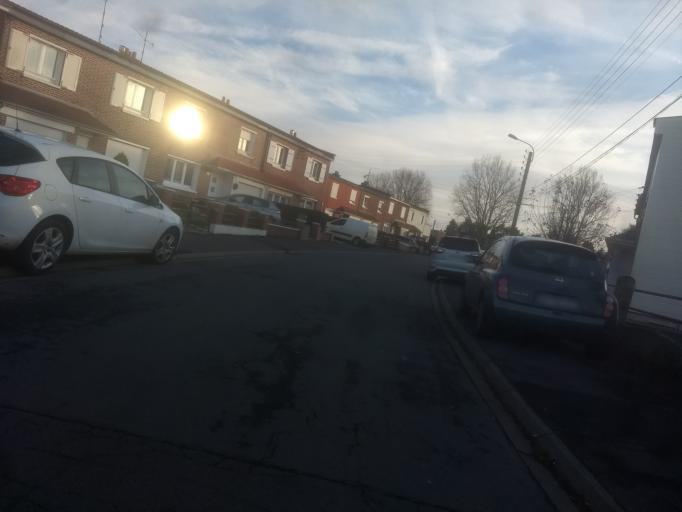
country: FR
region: Nord-Pas-de-Calais
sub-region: Departement du Pas-de-Calais
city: Beaurains
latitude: 50.2713
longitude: 2.7926
